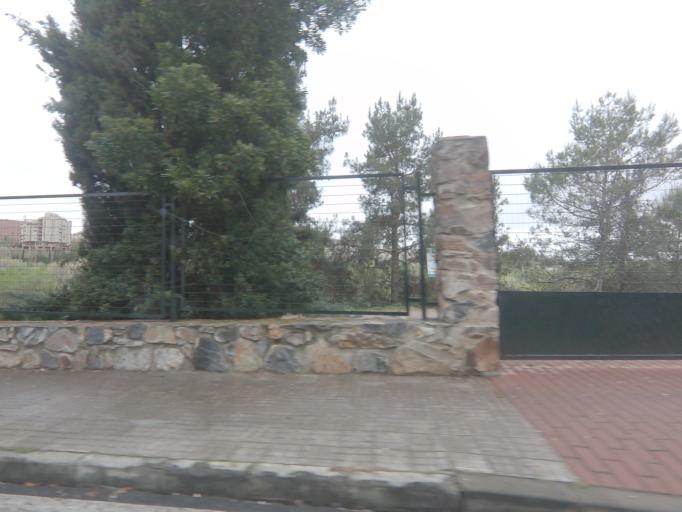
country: ES
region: Extremadura
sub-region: Provincia de Caceres
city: Caceres
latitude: 39.4730
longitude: -6.3820
